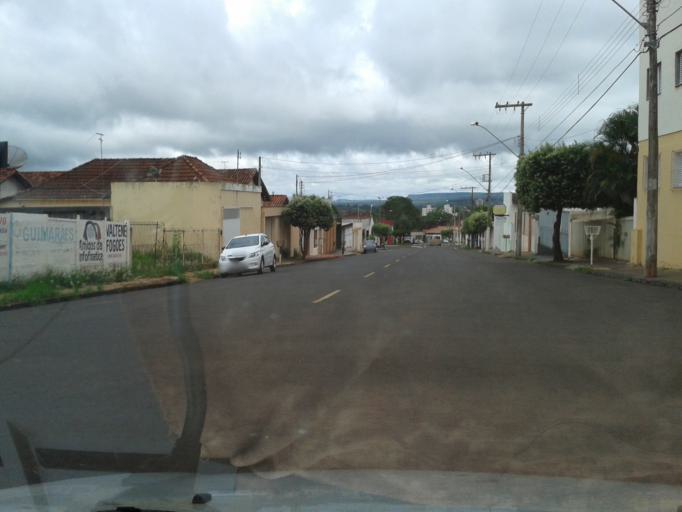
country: BR
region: Minas Gerais
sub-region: Ituiutaba
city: Ituiutaba
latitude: -18.9784
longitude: -49.4666
